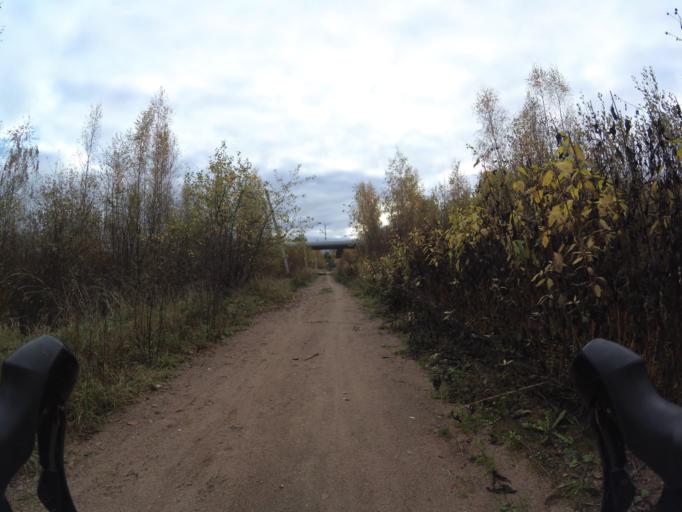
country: RU
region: St.-Petersburg
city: Lakhtinskiy
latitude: 60.0056
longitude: 30.1440
